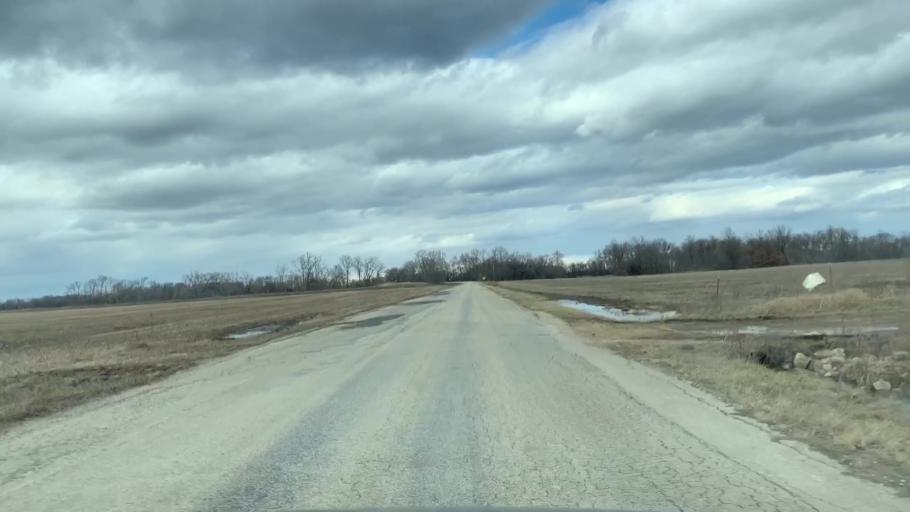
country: US
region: Kansas
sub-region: Allen County
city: Humboldt
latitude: 37.7983
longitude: -95.4706
